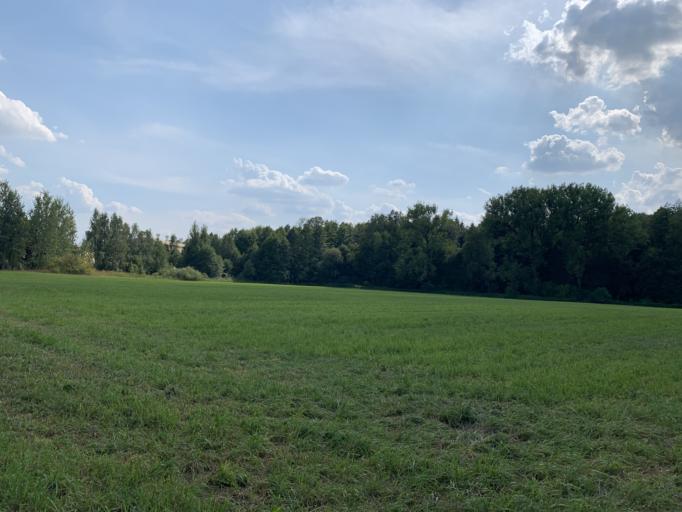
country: BY
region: Minsk
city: Nyasvizh
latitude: 53.2076
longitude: 26.6359
